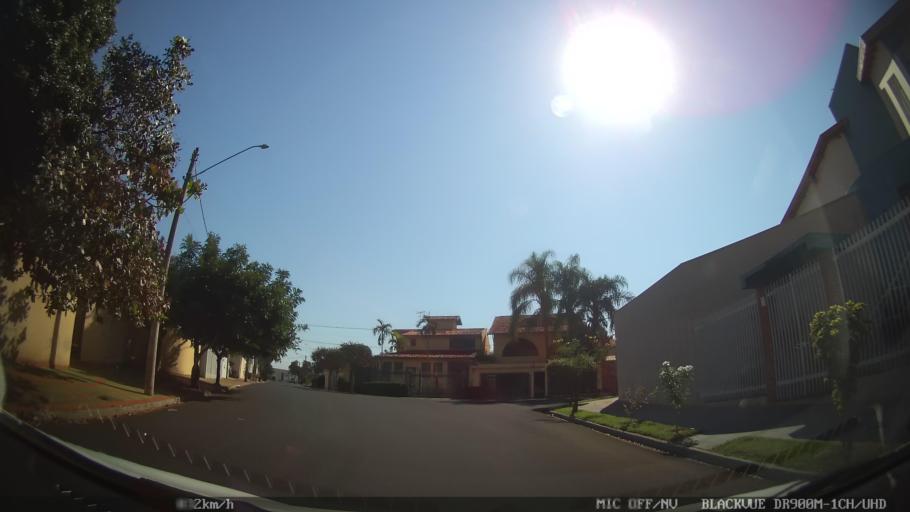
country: BR
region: Sao Paulo
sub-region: Ribeirao Preto
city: Ribeirao Preto
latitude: -21.2033
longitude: -47.7719
